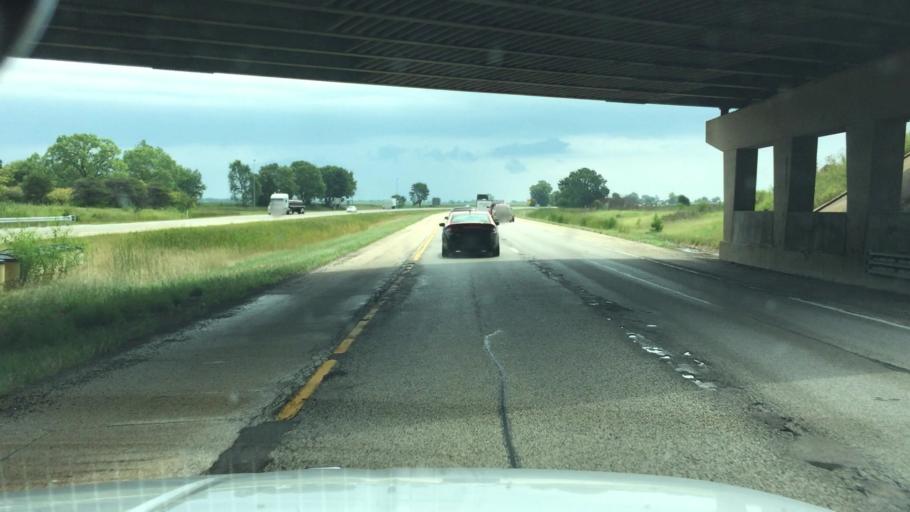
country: US
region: Illinois
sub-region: Peoria County
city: Elmwood
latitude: 40.8275
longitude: -89.8704
